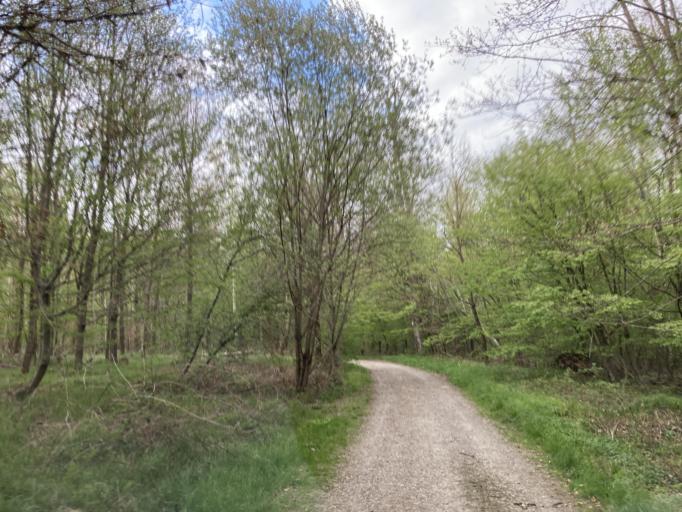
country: DE
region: Baden-Wuerttemberg
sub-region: Tuebingen Region
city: Wannweil
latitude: 48.5132
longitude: 9.1384
